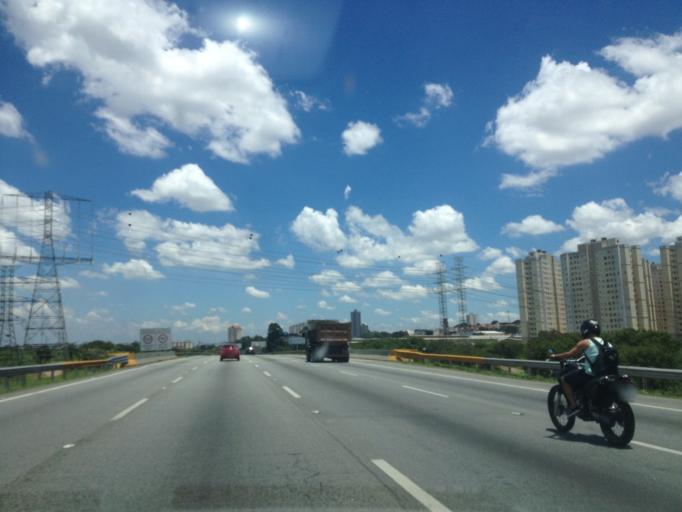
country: BR
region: Sao Paulo
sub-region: Guarulhos
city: Guarulhos
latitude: -23.4929
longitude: -46.5386
